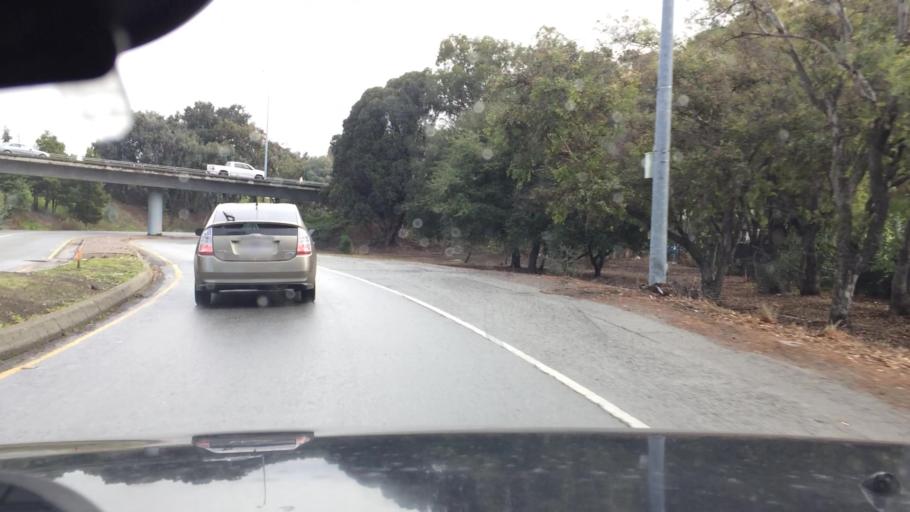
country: US
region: California
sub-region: San Mateo County
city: Redwood City
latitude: 37.4886
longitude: -122.2157
